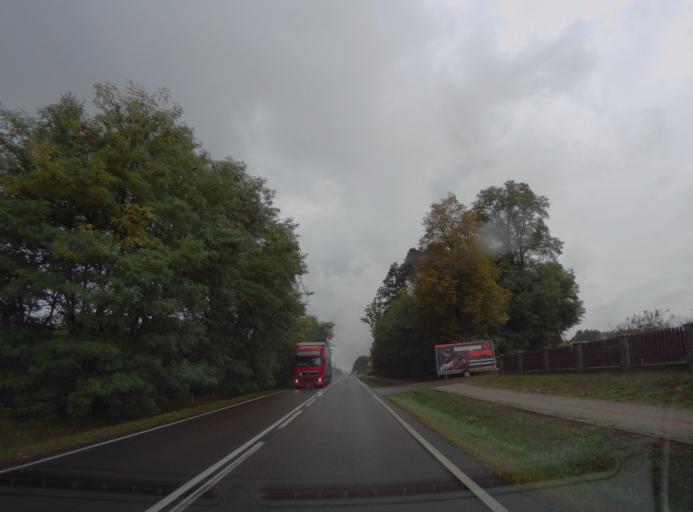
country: PL
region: Subcarpathian Voivodeship
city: Nowa Sarzyna
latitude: 50.3012
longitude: 22.3677
